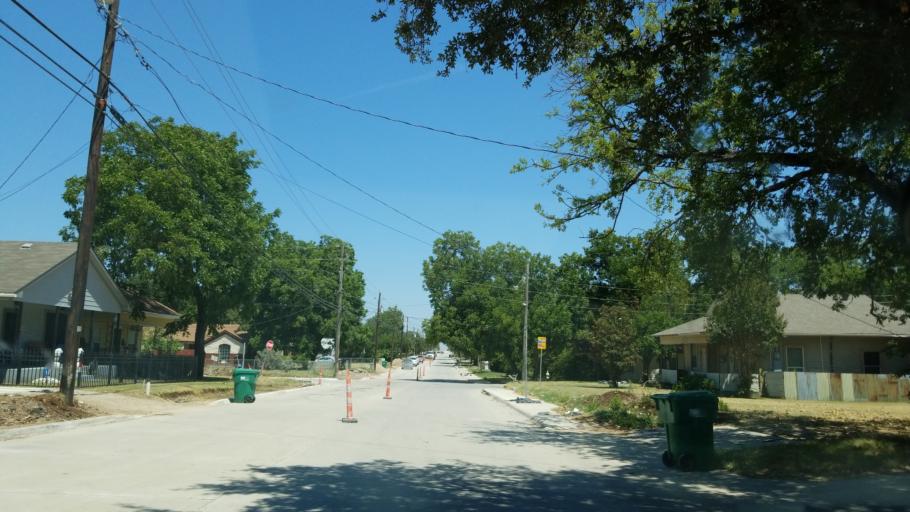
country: US
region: Texas
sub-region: Dallas County
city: Cockrell Hill
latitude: 32.7393
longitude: -96.8914
